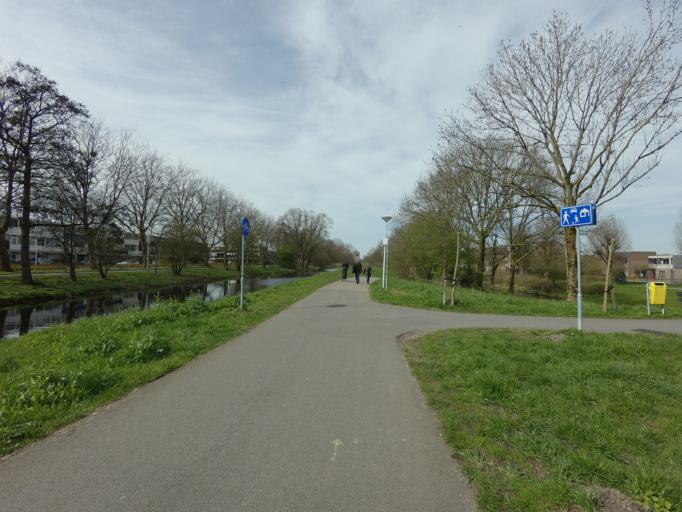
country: NL
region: South Holland
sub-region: Gemeente Alphen aan den Rijn
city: Alphen aan den Rijn
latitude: 52.1480
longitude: 4.6694
